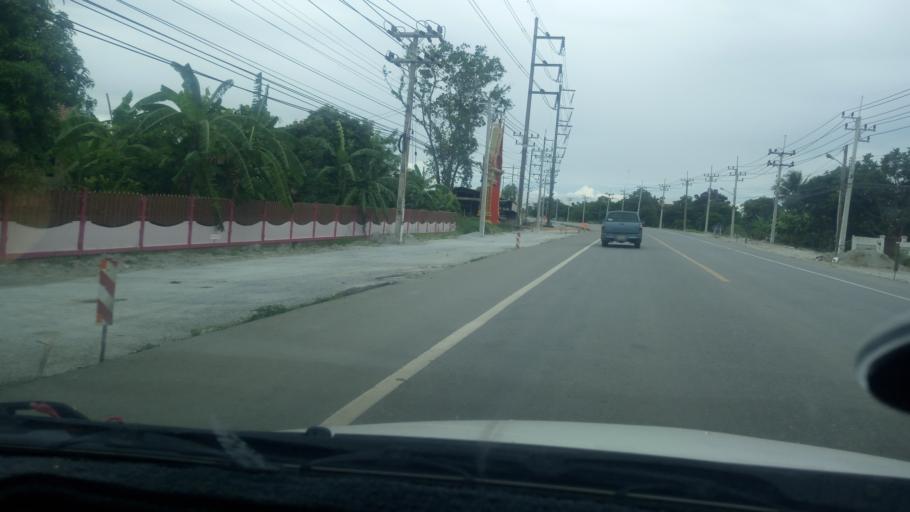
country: TH
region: Chon Buri
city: Phanat Nikhom
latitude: 13.5079
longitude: 101.1577
